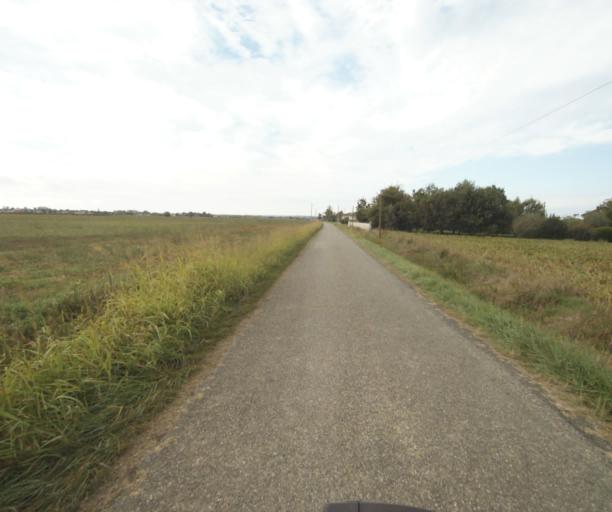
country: FR
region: Midi-Pyrenees
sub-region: Departement du Tarn-et-Garonne
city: Finhan
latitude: 43.9064
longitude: 1.2409
